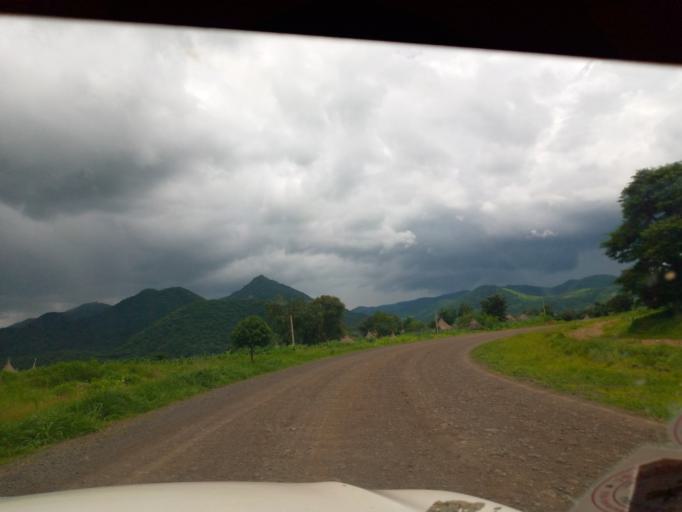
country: ET
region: Oromiya
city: Mendi
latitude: 10.1799
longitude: 35.0923
